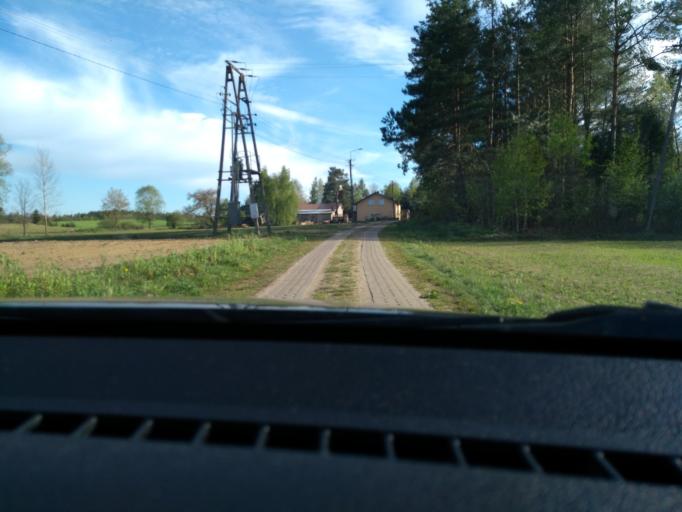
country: PL
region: Pomeranian Voivodeship
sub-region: Powiat leborski
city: Cewice
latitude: 54.3432
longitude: 17.6958
